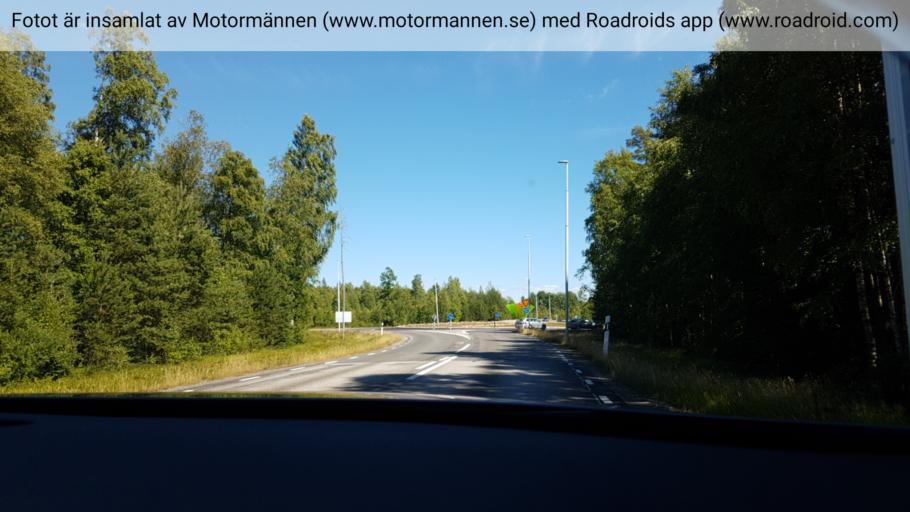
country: SE
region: Joenkoeping
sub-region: Gnosjo Kommun
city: Hillerstorp
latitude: 57.3165
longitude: 13.9074
